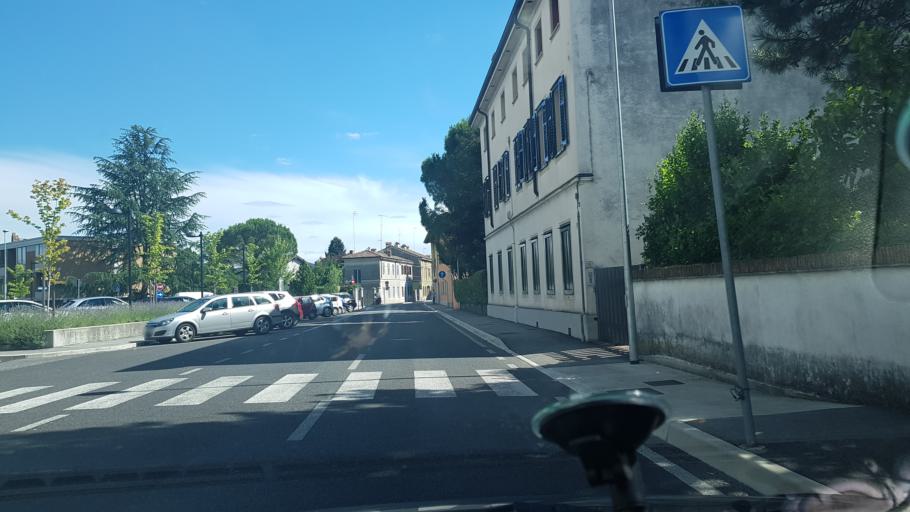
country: IT
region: Friuli Venezia Giulia
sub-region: Provincia di Gorizia
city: Gorizia
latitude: 45.9374
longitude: 13.6218
